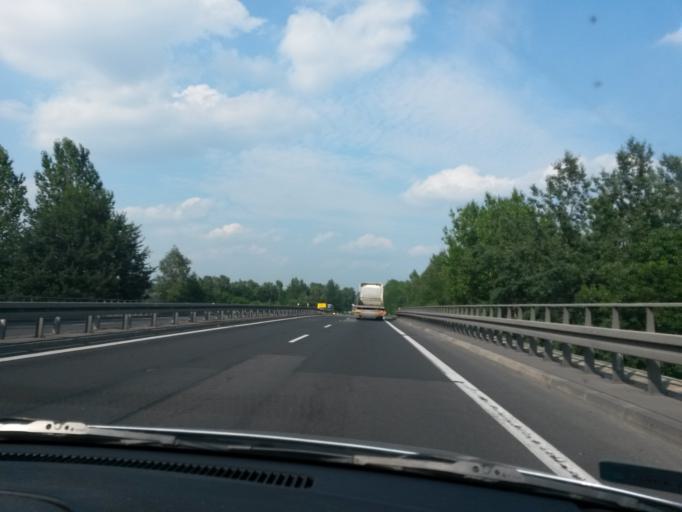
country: PL
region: Silesian Voivodeship
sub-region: Myslowice
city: Myslowice
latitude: 50.2468
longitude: 19.1761
